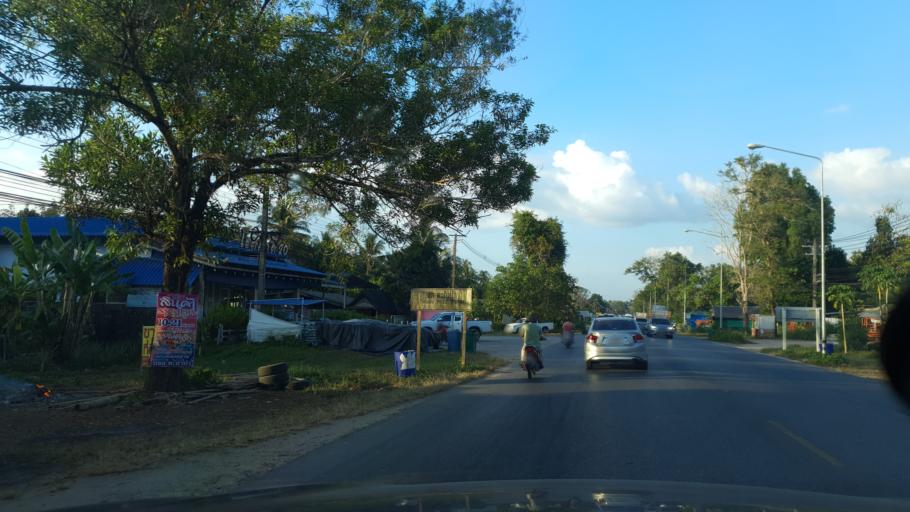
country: TH
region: Phangnga
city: Takua Pa
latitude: 8.8347
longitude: 98.2835
